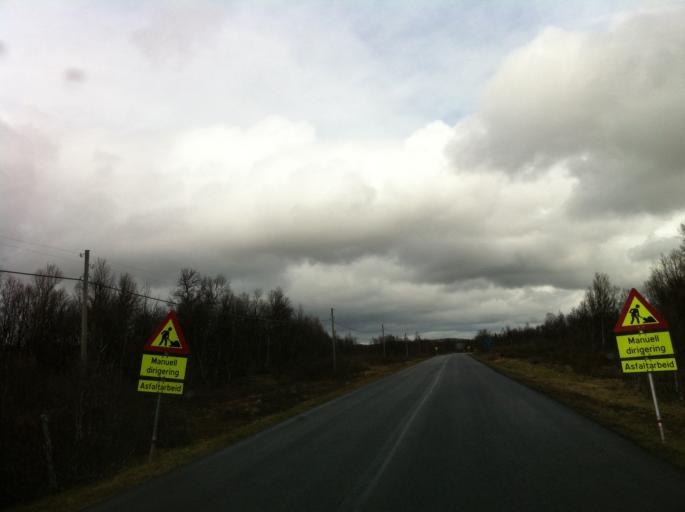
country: NO
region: Sor-Trondelag
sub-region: Tydal
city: Aas
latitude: 62.6373
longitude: 11.9950
